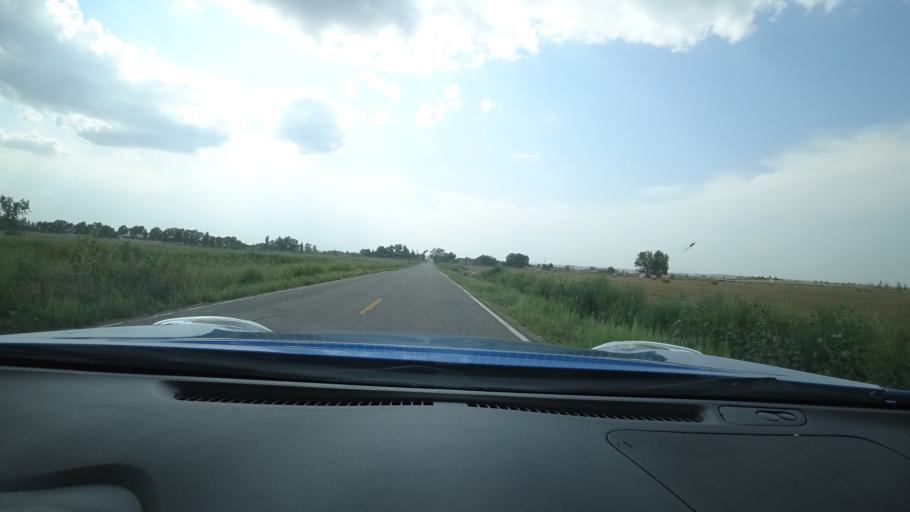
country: US
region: Colorado
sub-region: Adams County
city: Brighton
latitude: 39.9216
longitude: -104.8245
